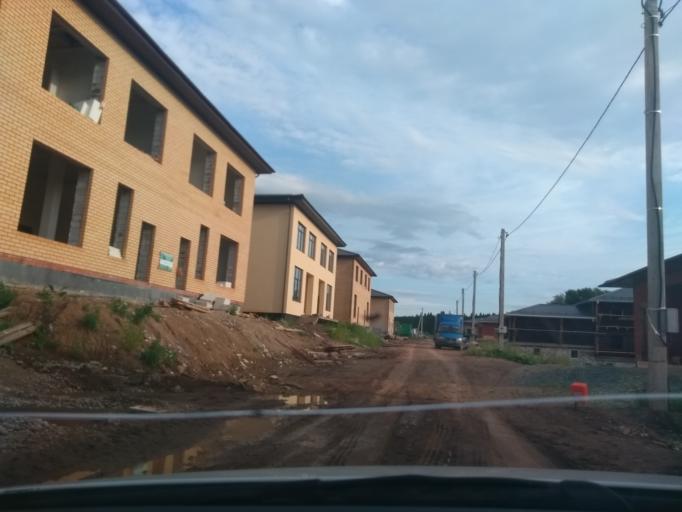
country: RU
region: Perm
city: Perm
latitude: 57.9993
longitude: 56.3217
